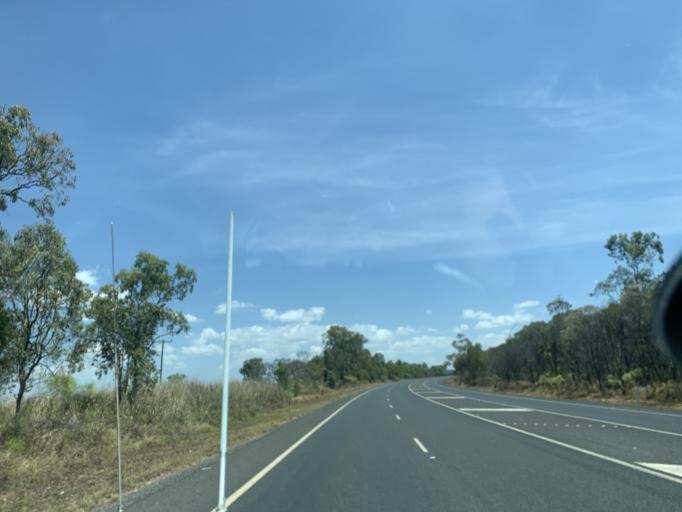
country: AU
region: Queensland
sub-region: Tablelands
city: Mareeba
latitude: -16.9812
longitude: 145.5306
